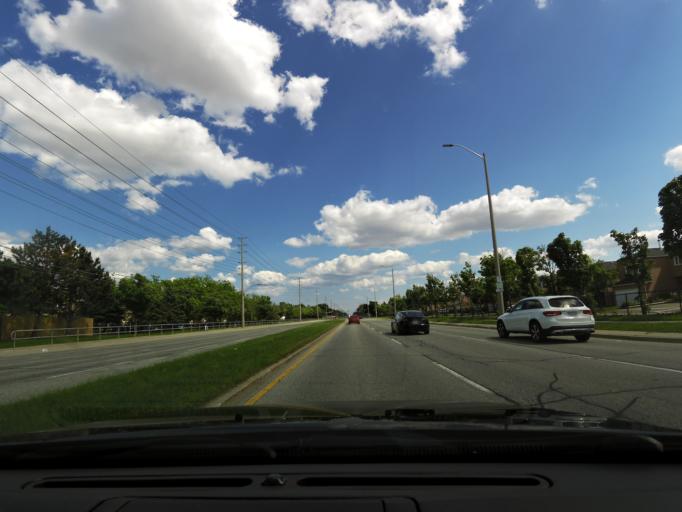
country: CA
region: Ontario
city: Brampton
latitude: 43.5942
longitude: -79.7795
